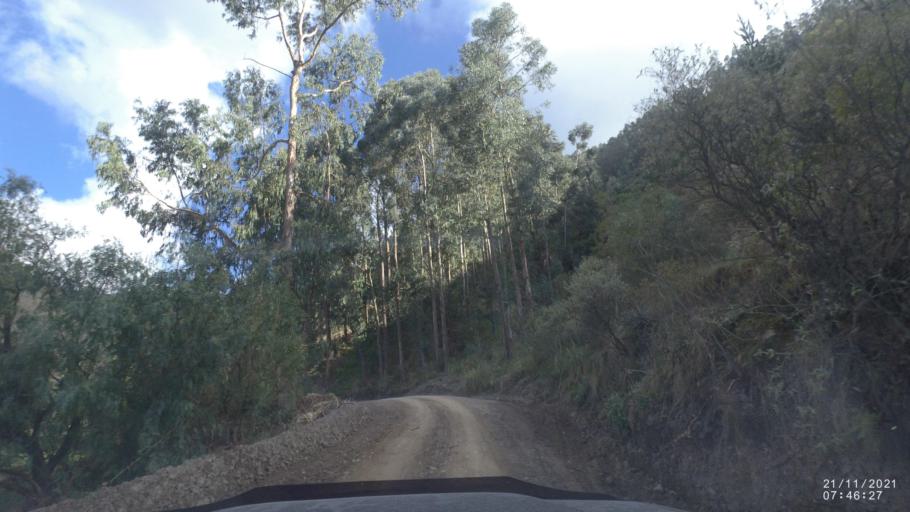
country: BO
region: Cochabamba
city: Cochabamba
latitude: -17.3115
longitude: -66.2192
